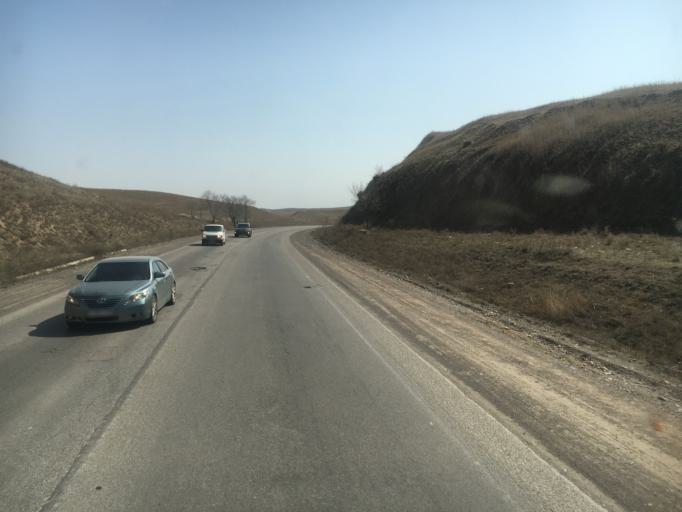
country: KZ
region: Almaty Oblysy
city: Burunday
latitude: 43.3041
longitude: 76.2200
